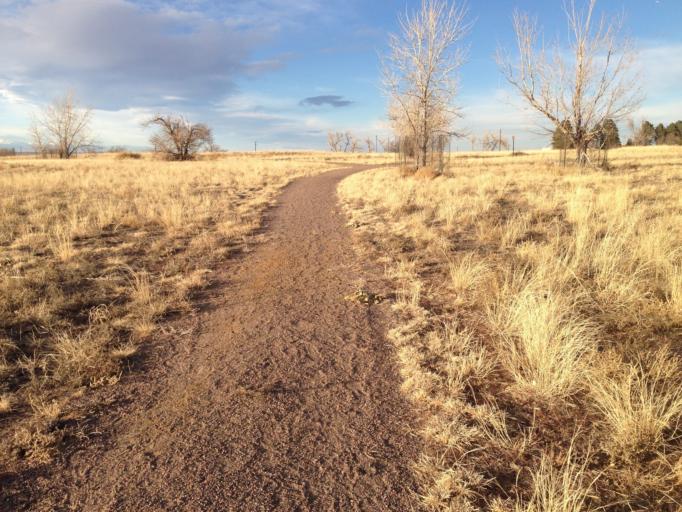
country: US
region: Colorado
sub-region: Adams County
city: Derby
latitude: 39.8247
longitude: -104.8607
